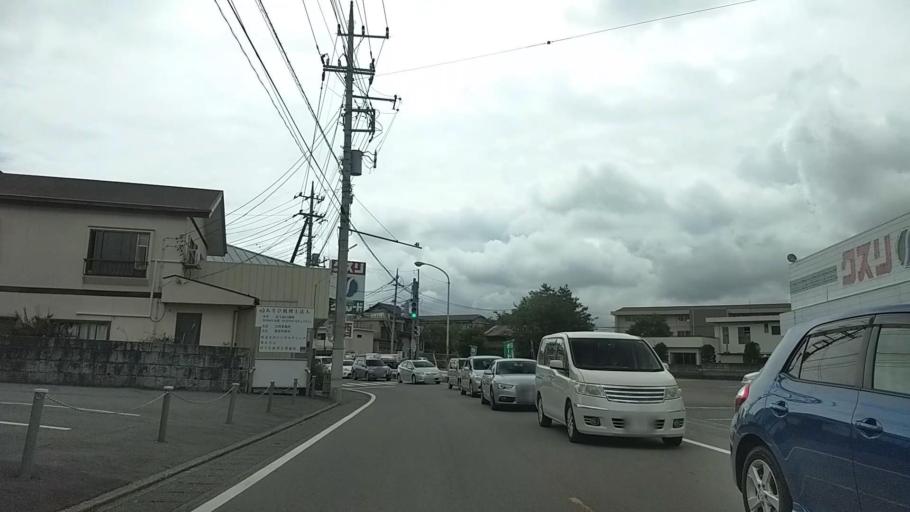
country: JP
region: Yamanashi
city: Fujikawaguchiko
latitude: 35.5018
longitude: 138.7594
